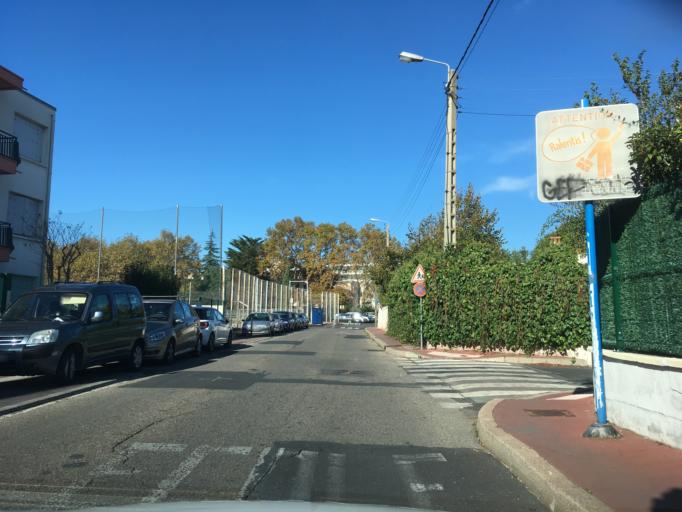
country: FR
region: Languedoc-Roussillon
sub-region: Departement de l'Herault
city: Juvignac
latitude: 43.6123
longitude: 3.8330
